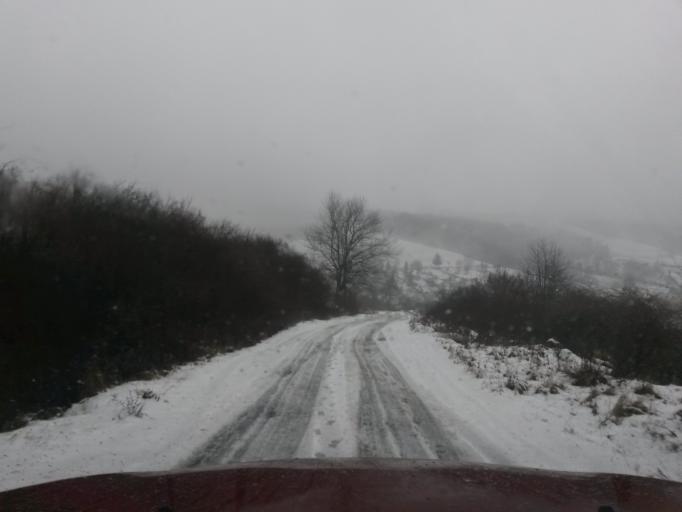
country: SK
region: Presovsky
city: Stropkov
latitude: 49.2450
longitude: 21.7486
